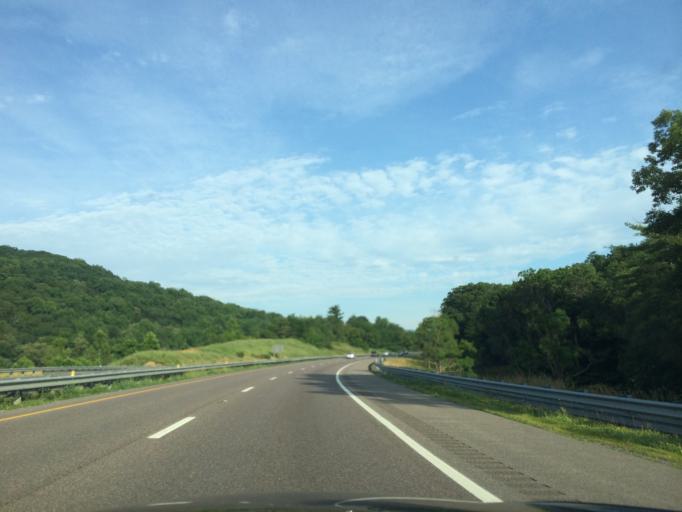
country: US
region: Maryland
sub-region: Allegany County
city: Cumberland
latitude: 39.6979
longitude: -78.5571
